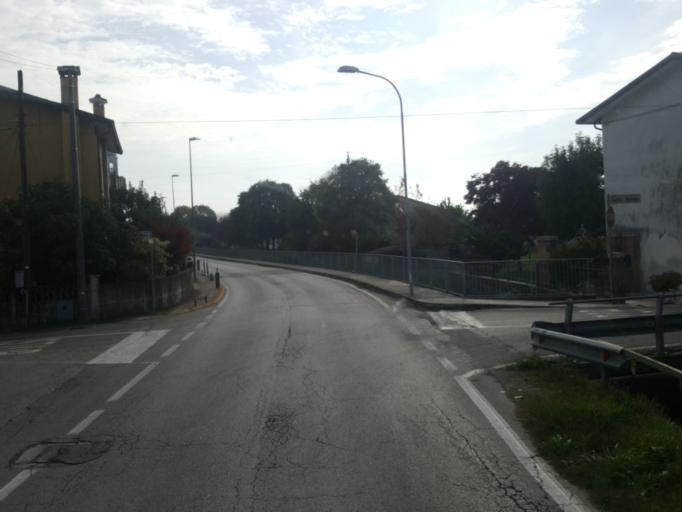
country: IT
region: Veneto
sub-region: Provincia di Treviso
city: Ca' Rainati
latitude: 45.7380
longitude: 11.8424
